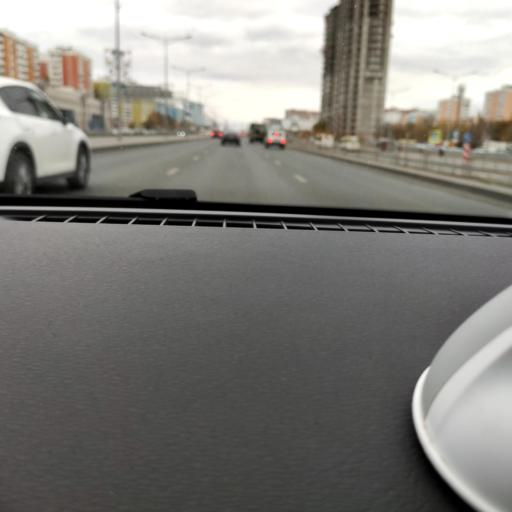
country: RU
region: Samara
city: Samara
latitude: 53.2534
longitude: 50.2268
